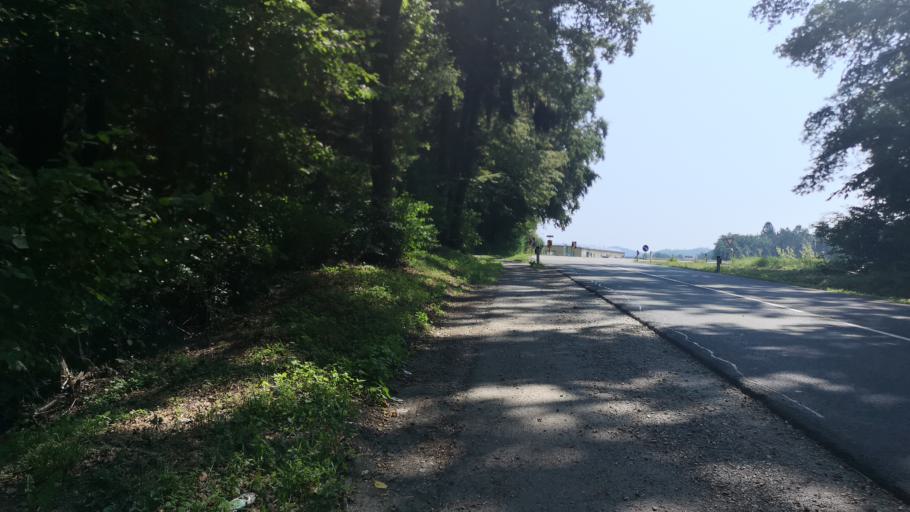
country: AT
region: Styria
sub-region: Politischer Bezirk Deutschlandsberg
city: Preding
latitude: 46.8577
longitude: 15.3929
